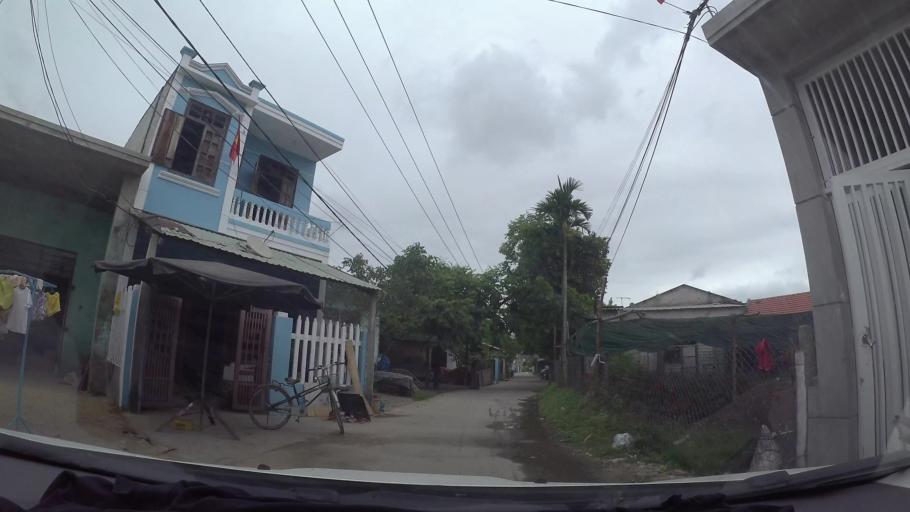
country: VN
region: Da Nang
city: Lien Chieu
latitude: 16.0866
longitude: 108.1024
